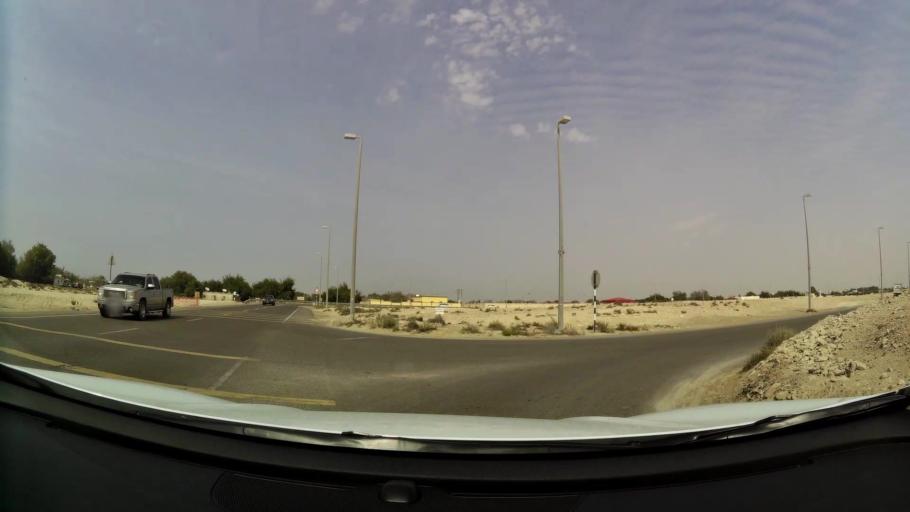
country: AE
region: Abu Dhabi
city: Abu Dhabi
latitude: 24.5643
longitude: 54.6790
